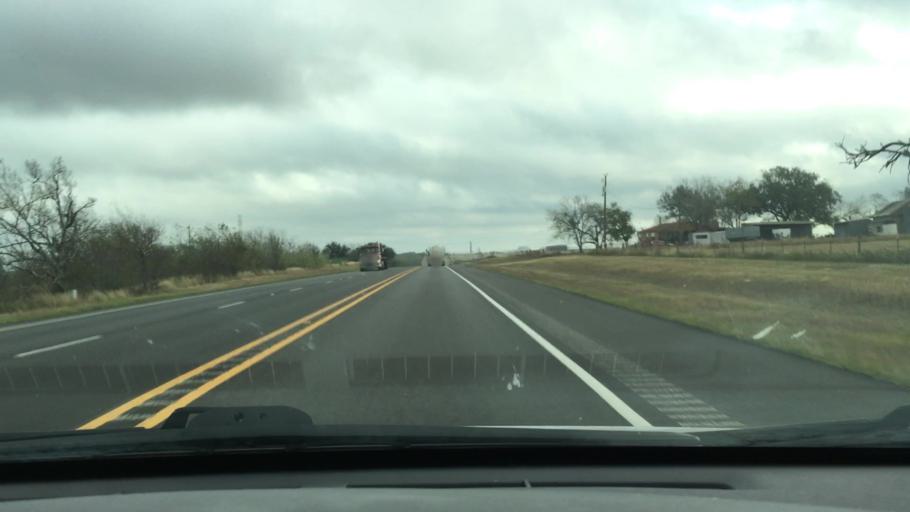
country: US
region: Texas
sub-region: Gonzales County
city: Nixon
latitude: 29.2564
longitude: -97.8126
